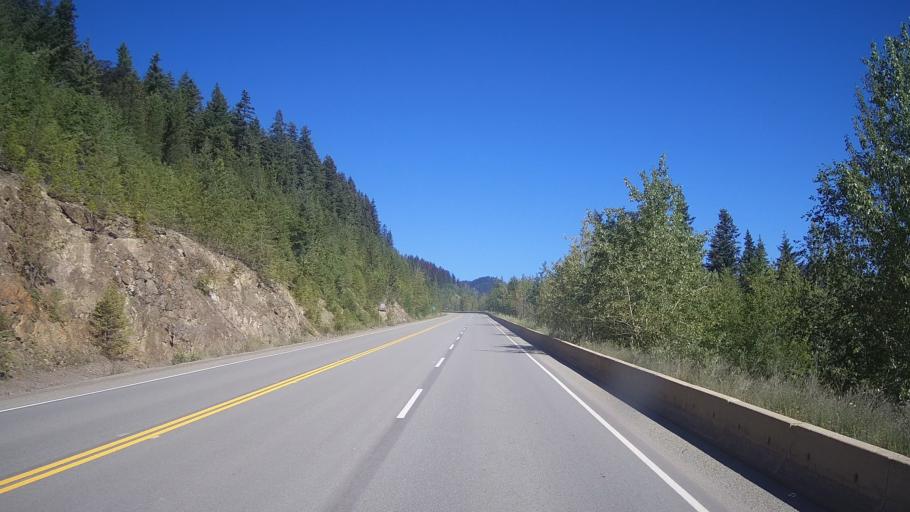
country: CA
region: British Columbia
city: Kamloops
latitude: 51.4787
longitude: -120.2590
